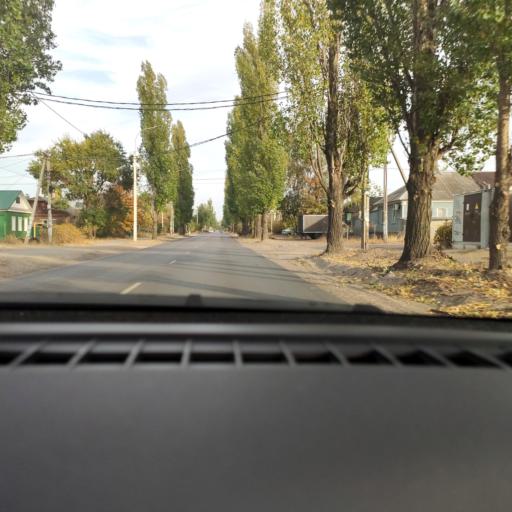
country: RU
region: Voronezj
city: Somovo
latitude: 51.7393
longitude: 39.2735
